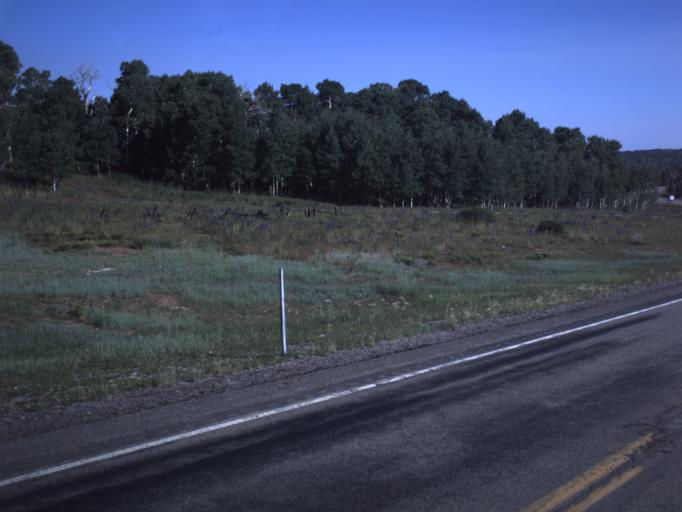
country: US
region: Utah
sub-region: Sanpete County
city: Fairview
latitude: 39.6490
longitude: -111.3287
